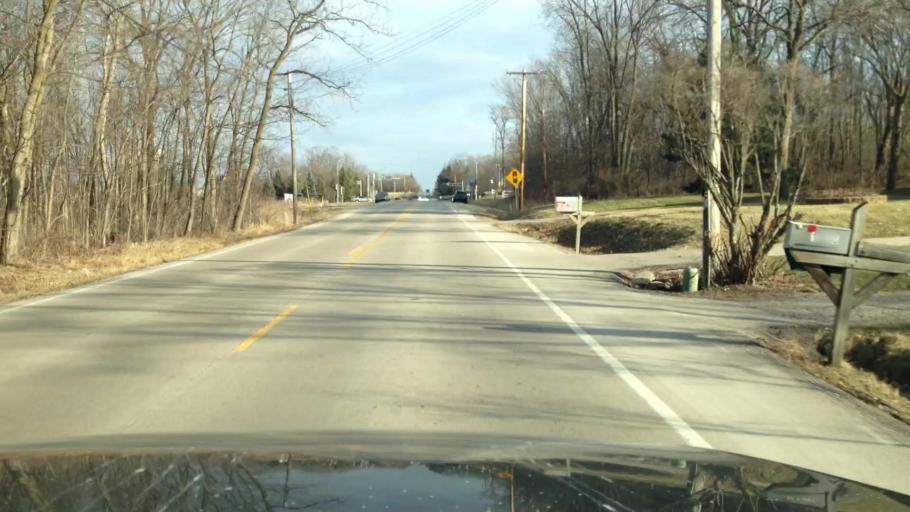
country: US
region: Wisconsin
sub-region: Waukesha County
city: Muskego
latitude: 42.9300
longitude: -88.1172
